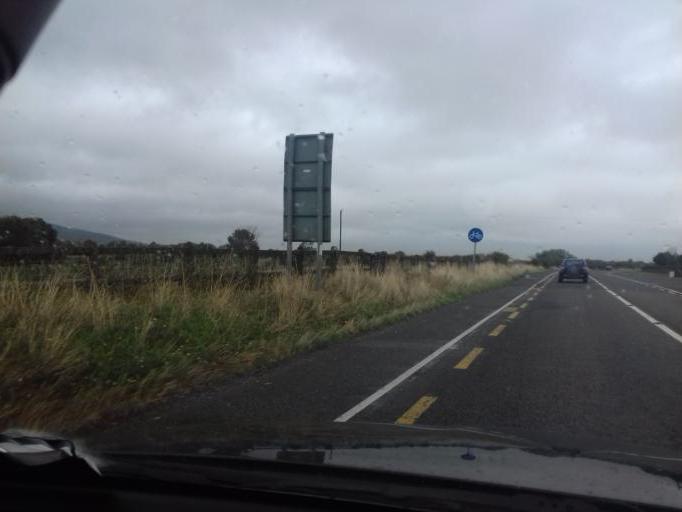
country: IE
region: Leinster
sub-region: County Carlow
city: Bagenalstown
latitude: 52.7473
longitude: -6.9674
